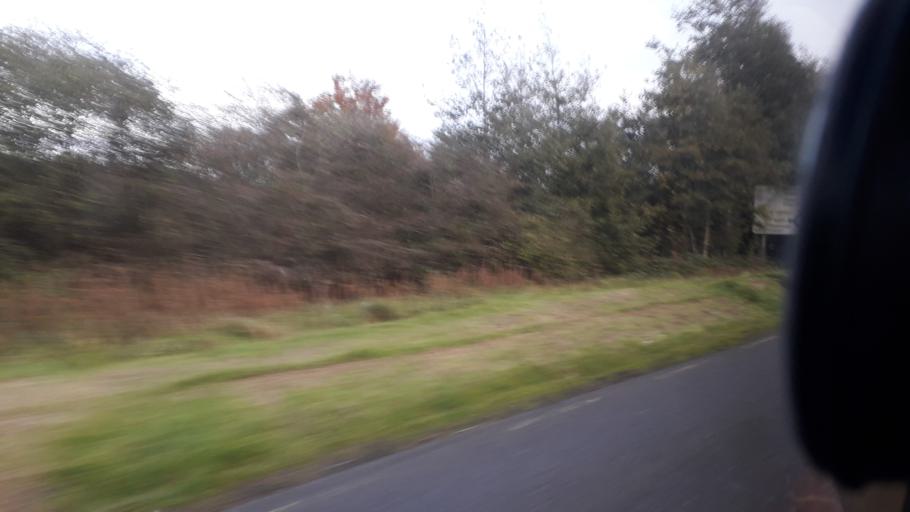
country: IE
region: Munster
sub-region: An Clar
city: Shannon
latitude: 52.7124
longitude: -8.8838
